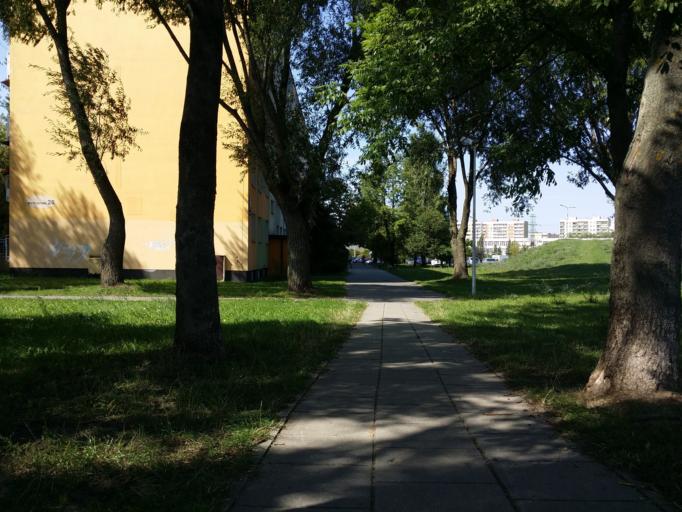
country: PL
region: Masovian Voivodeship
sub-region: Radom
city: Radom
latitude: 51.3754
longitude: 21.1655
